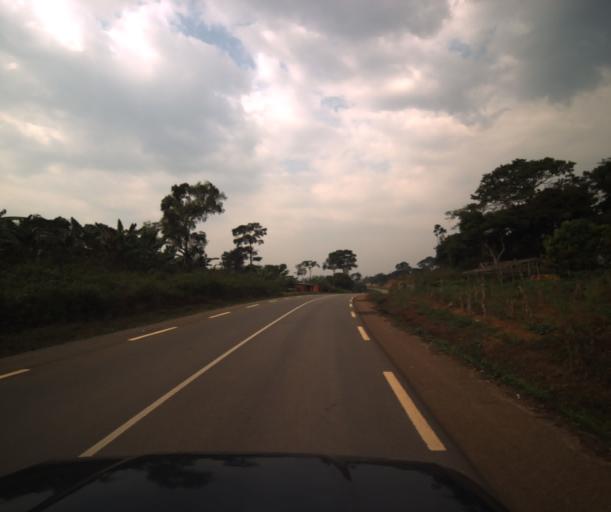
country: CM
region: Centre
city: Mbankomo
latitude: 3.7503
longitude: 11.4019
